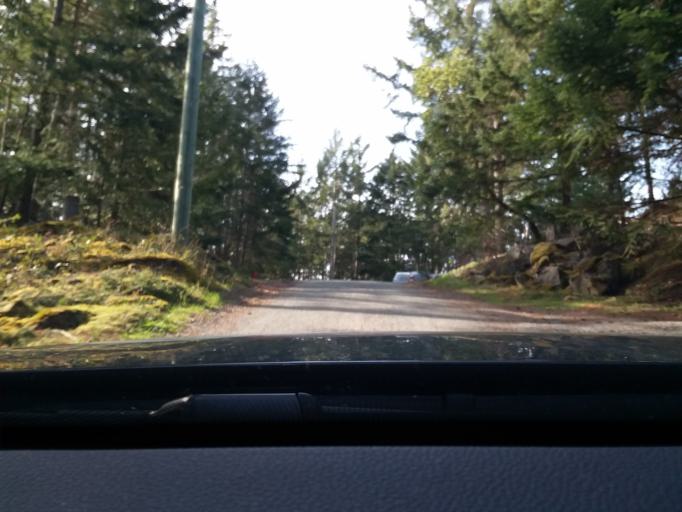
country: CA
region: British Columbia
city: North Saanich
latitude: 48.7710
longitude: -123.2947
